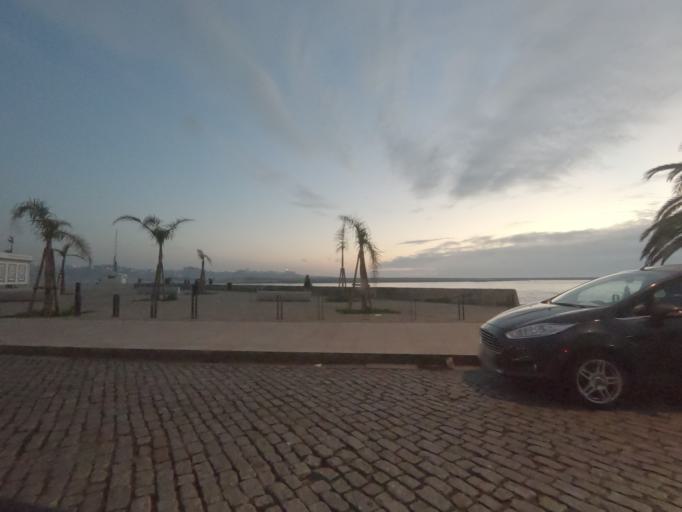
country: PT
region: Porto
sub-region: Vila Nova de Gaia
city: Canidelo
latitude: 41.1476
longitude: -8.6674
